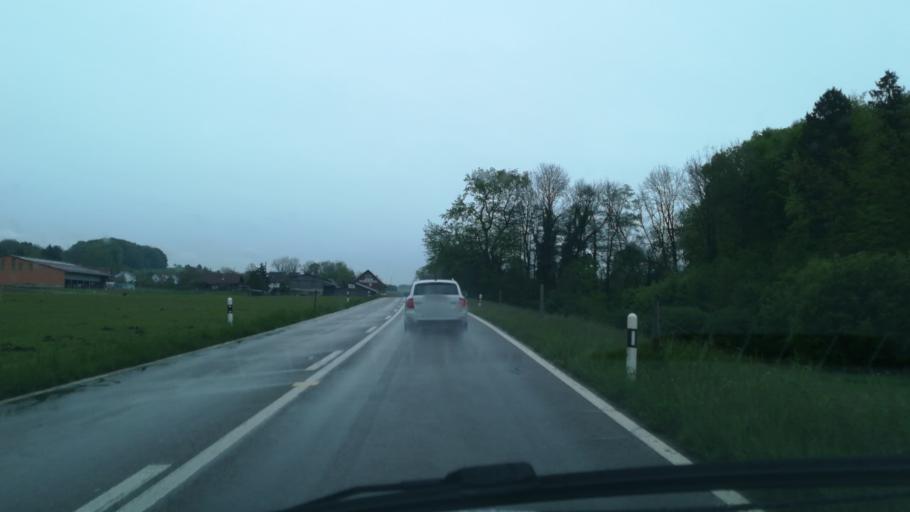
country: CH
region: Thurgau
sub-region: Weinfelden District
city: Wigoltingen
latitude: 47.6101
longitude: 9.0326
